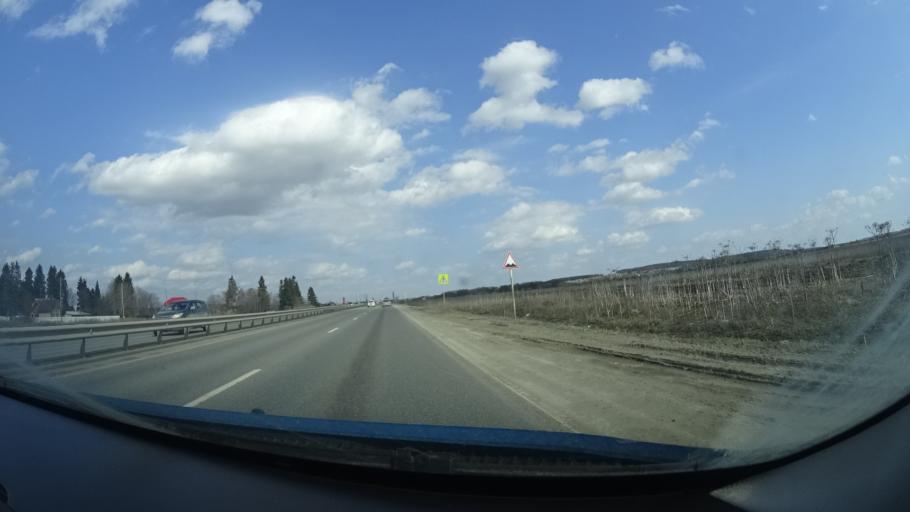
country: RU
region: Perm
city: Kultayevo
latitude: 57.8950
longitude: 55.9596
